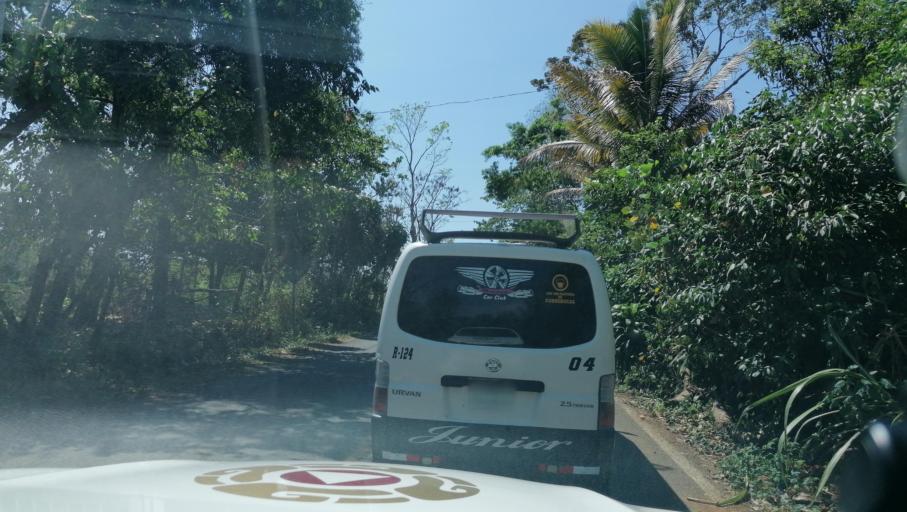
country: MX
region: Chiapas
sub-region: Cacahoatan
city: Benito Juarez
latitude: 15.0165
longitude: -92.2262
